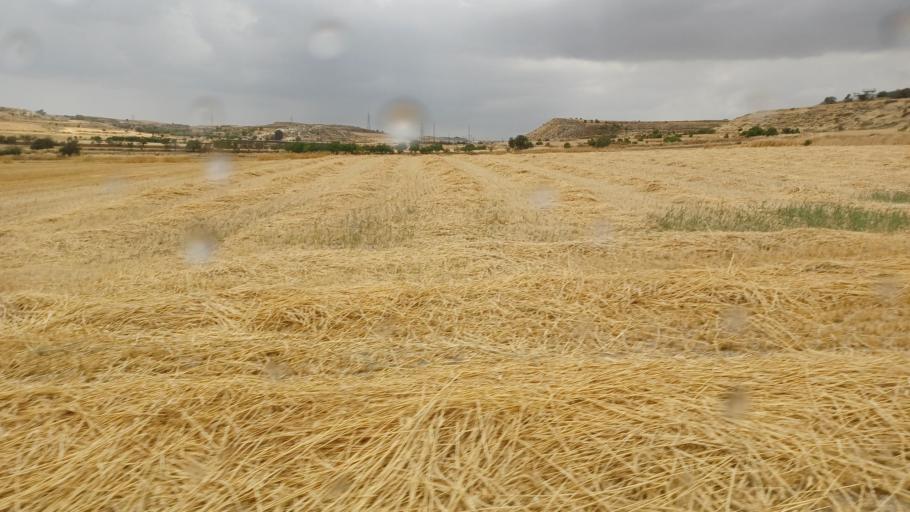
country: CY
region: Larnaka
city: Athienou
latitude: 35.0430
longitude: 33.5675
